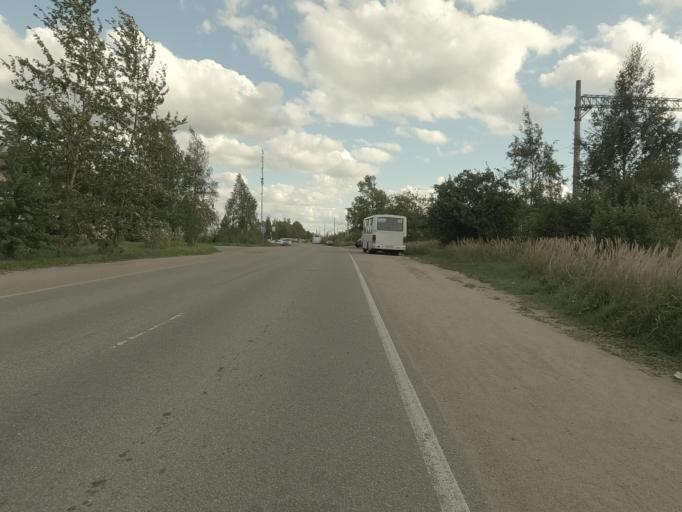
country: RU
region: Leningrad
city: Ul'yanovka
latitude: 59.6349
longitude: 30.7593
